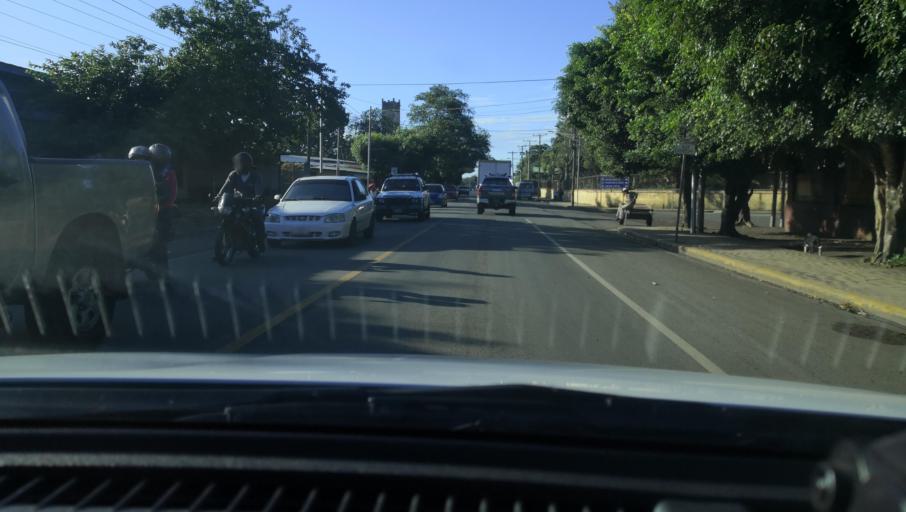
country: NI
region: Carazo
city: Jinotepe
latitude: 11.8509
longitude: -86.1961
